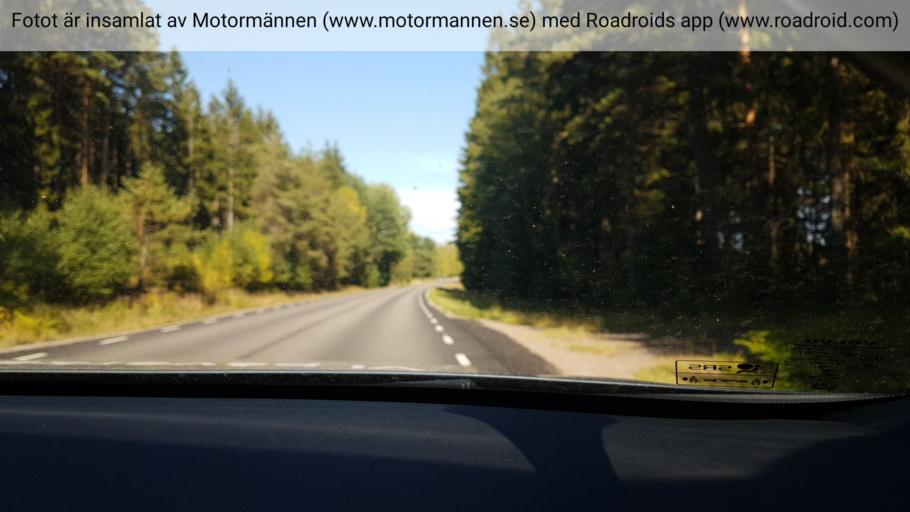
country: SE
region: Vaestra Goetaland
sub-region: Gotene Kommun
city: Goetene
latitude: 58.6214
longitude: 13.5922
